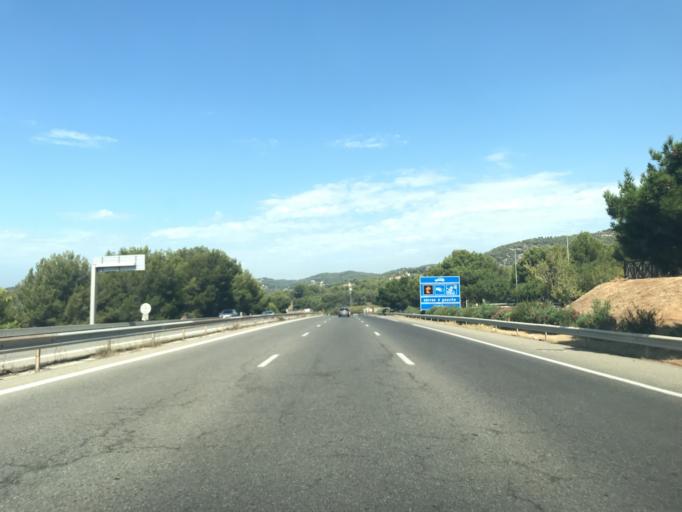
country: FR
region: Provence-Alpes-Cote d'Azur
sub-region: Departement du Var
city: Sanary-sur-Mer
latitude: 43.1434
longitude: 5.7881
